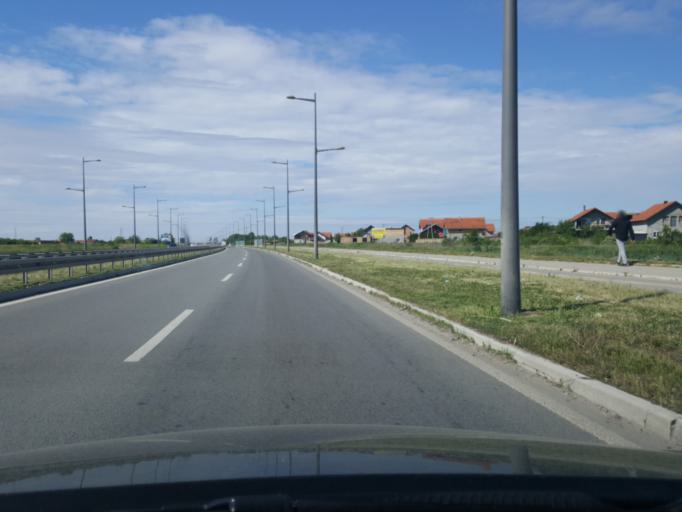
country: RS
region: Autonomna Pokrajina Vojvodina
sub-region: Juznobacki Okrug
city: Novi Sad
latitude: 45.2926
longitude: 19.8084
